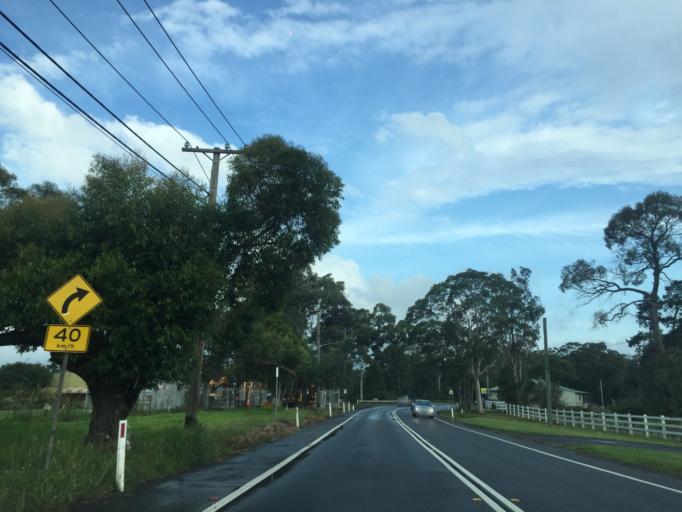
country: AU
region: New South Wales
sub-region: Hornsby Shire
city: Galston
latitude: -33.6563
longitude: 151.0400
